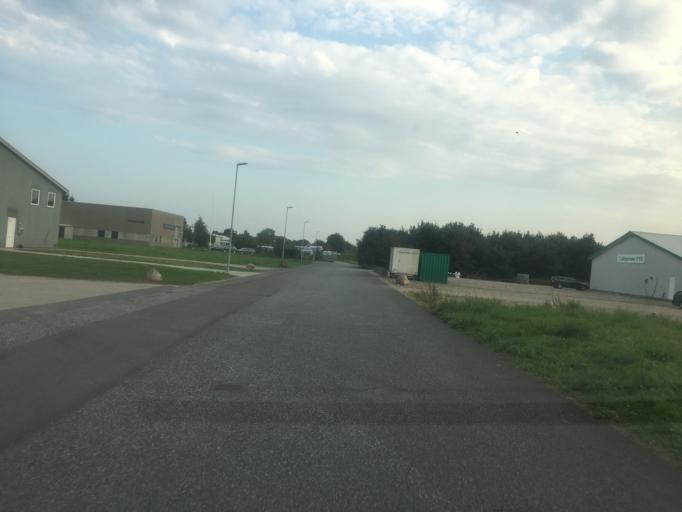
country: DK
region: South Denmark
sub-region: Tonder Kommune
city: Tonder
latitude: 54.9496
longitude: 8.8662
